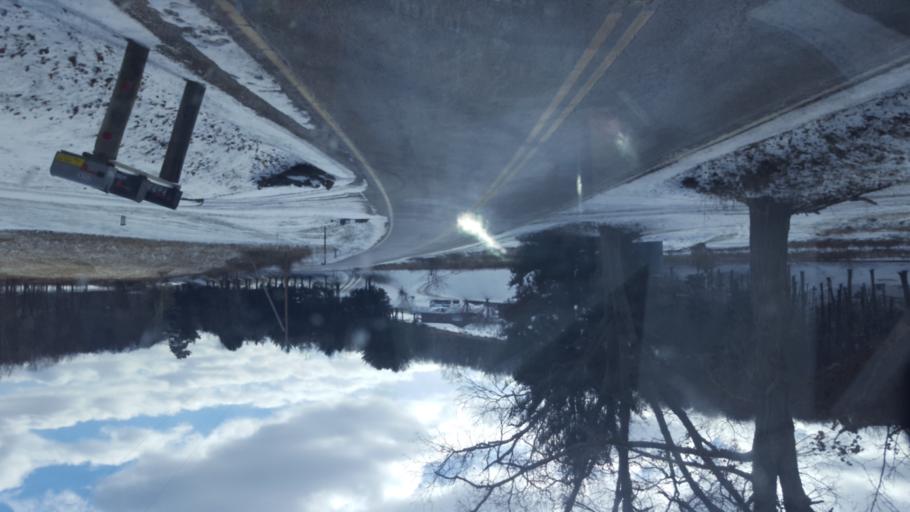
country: US
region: Ohio
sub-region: Coshocton County
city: West Lafayette
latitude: 40.3195
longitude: -81.7894
